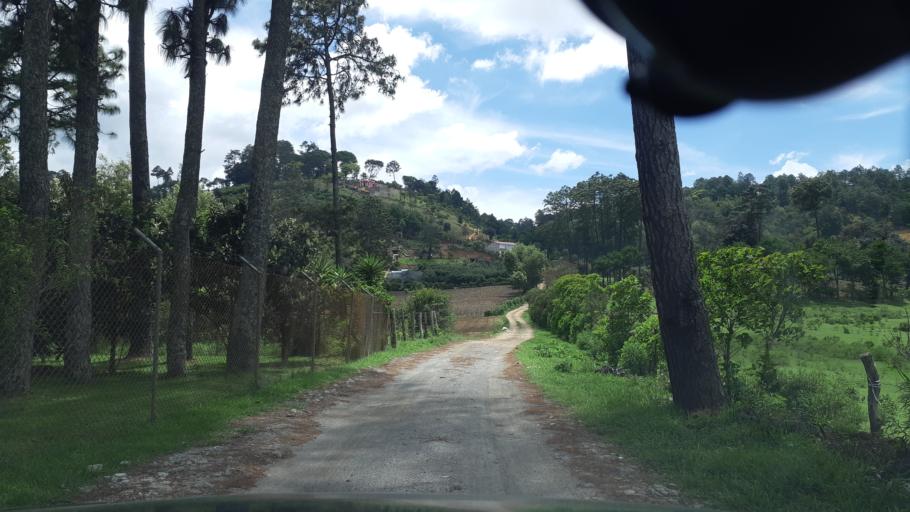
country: GT
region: Chimaltenango
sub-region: Municipio de Chimaltenango
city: Chimaltenango
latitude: 14.6608
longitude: -90.8470
